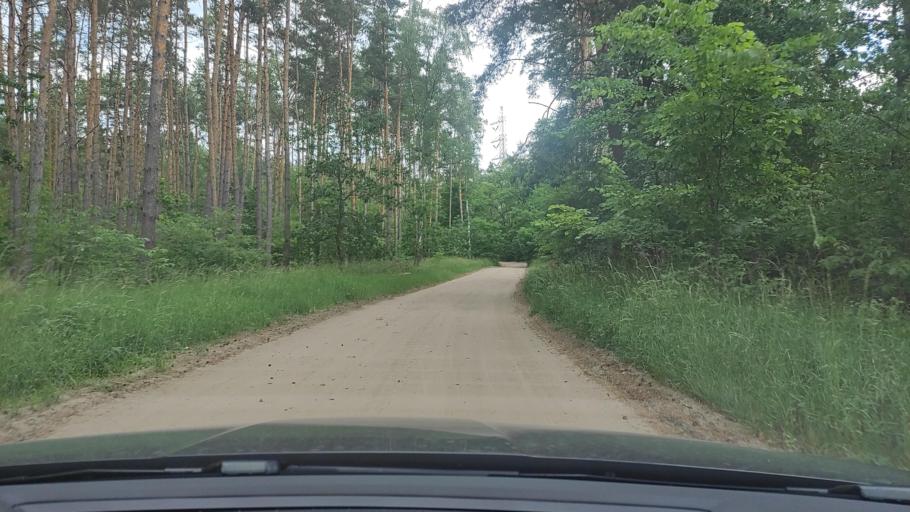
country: PL
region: Greater Poland Voivodeship
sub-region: Powiat poznanski
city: Pobiedziska
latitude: 52.4976
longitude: 17.2016
